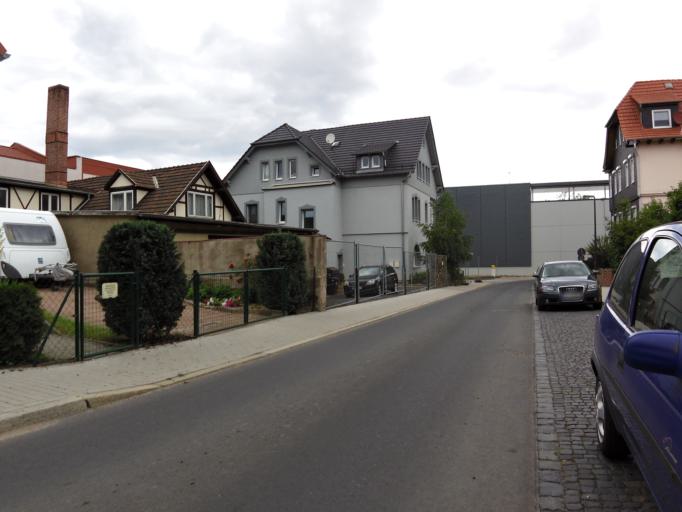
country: DE
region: Thuringia
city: Bad Salzungen
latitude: 50.8138
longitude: 10.2284
